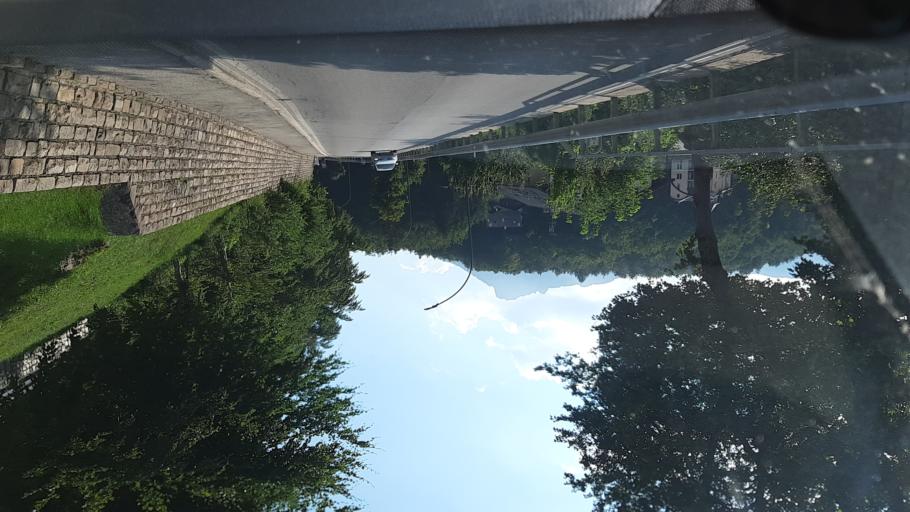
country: IT
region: Trentino-Alto Adige
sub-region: Provincia di Trento
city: Gionghi-Cappella
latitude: 45.9417
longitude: 11.2505
